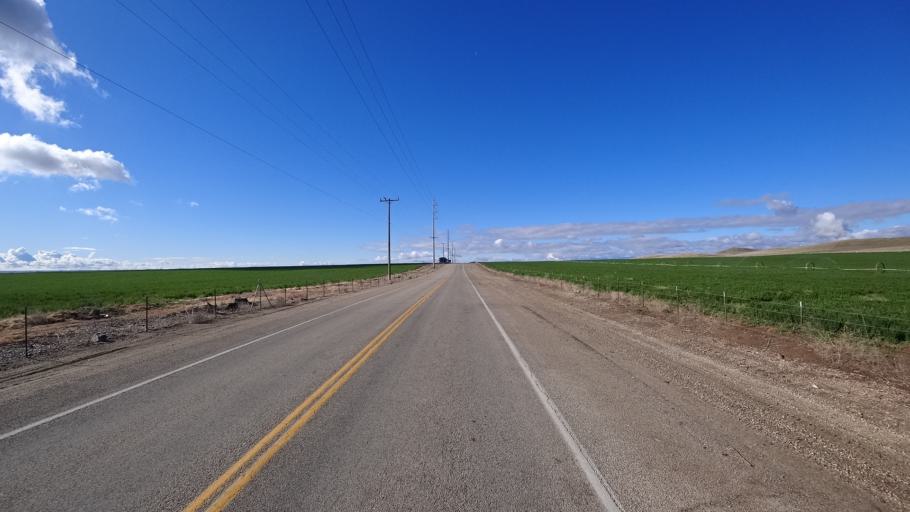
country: US
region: Idaho
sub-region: Ada County
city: Kuna
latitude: 43.4502
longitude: -116.4139
